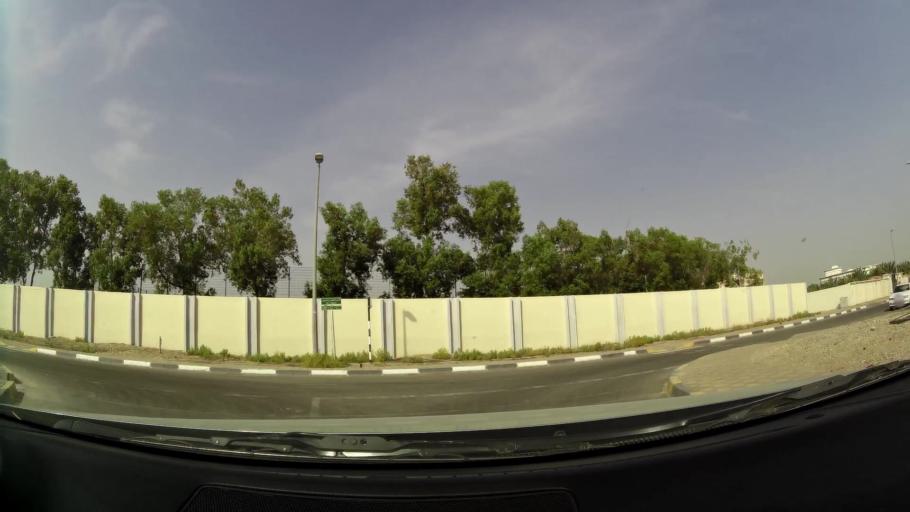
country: AE
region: Abu Dhabi
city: Al Ain
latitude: 24.1426
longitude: 55.6938
